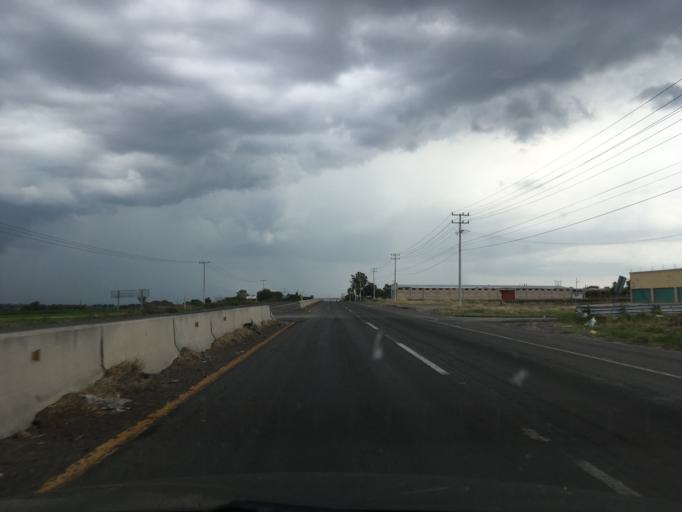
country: MX
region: Guanajuato
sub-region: Celaya
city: El Sauz (El Sauz de Villasenor)
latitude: 20.3938
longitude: -100.7900
